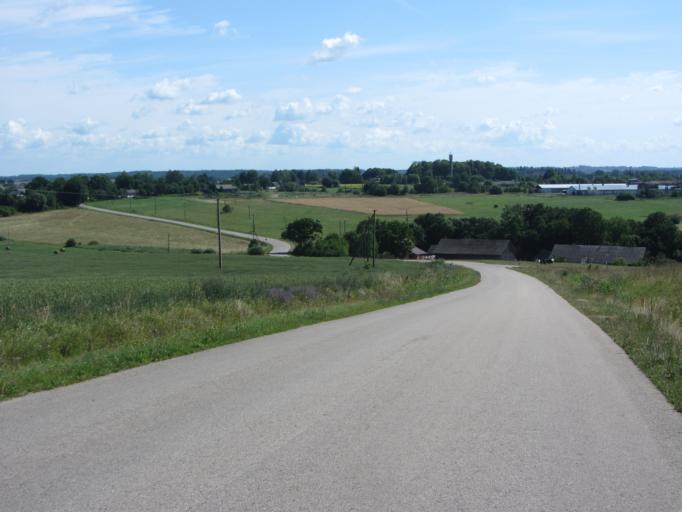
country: LT
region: Vilnius County
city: Elektrenai
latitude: 54.8981
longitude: 24.7102
